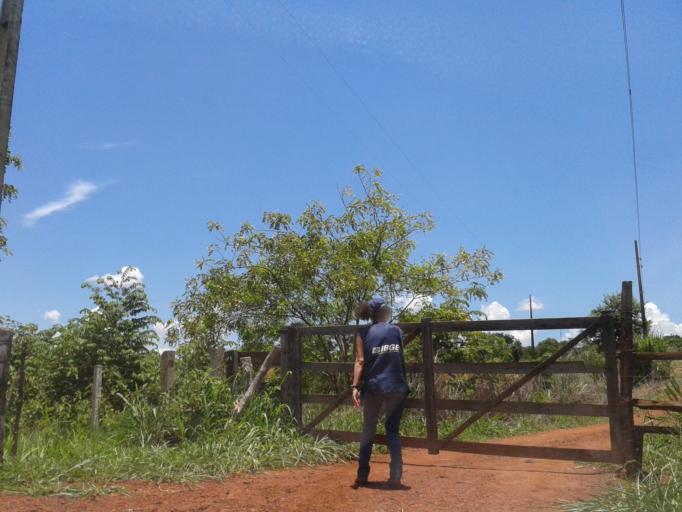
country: BR
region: Minas Gerais
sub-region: Santa Vitoria
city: Santa Vitoria
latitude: -19.1245
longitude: -50.5637
